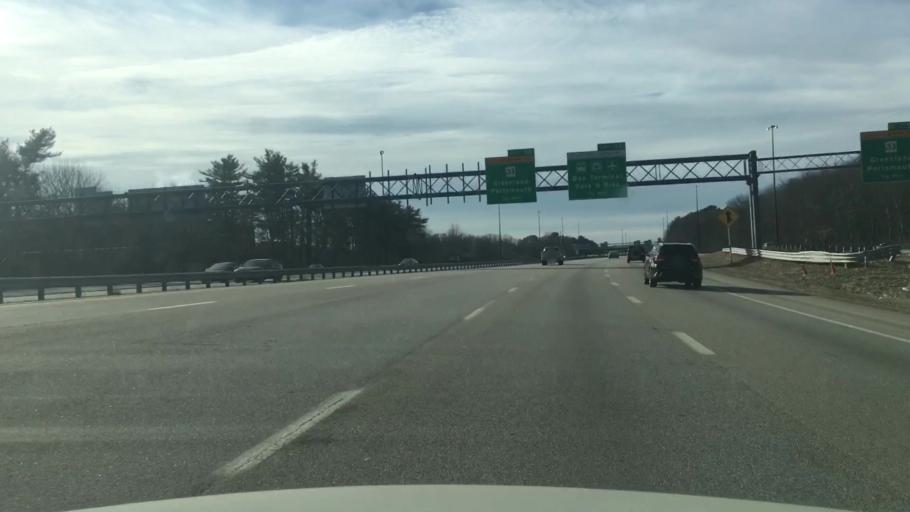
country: US
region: New Hampshire
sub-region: Rockingham County
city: Portsmouth
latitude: 43.0663
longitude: -70.7919
